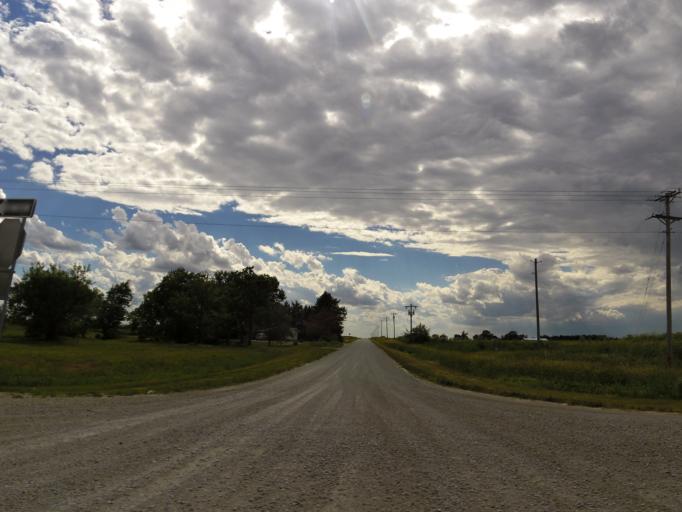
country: US
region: Iowa
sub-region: Henry County
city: Mount Pleasant
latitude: 40.7446
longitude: -91.5641
